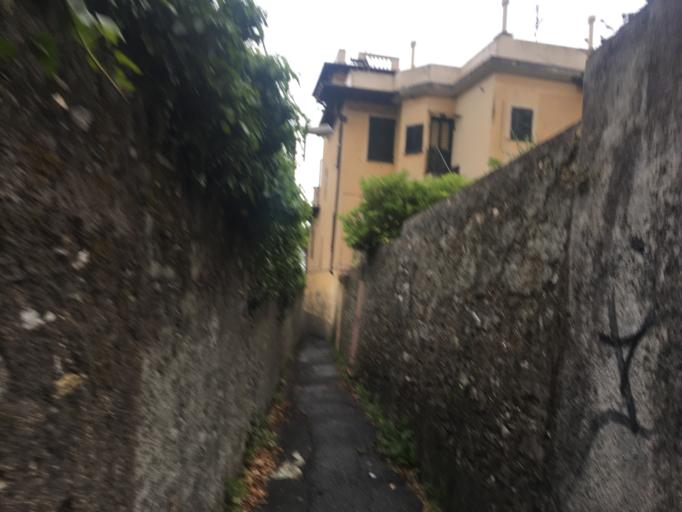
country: IT
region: Liguria
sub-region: Provincia di Genova
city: Bogliasco
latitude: 44.3827
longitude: 9.0362
